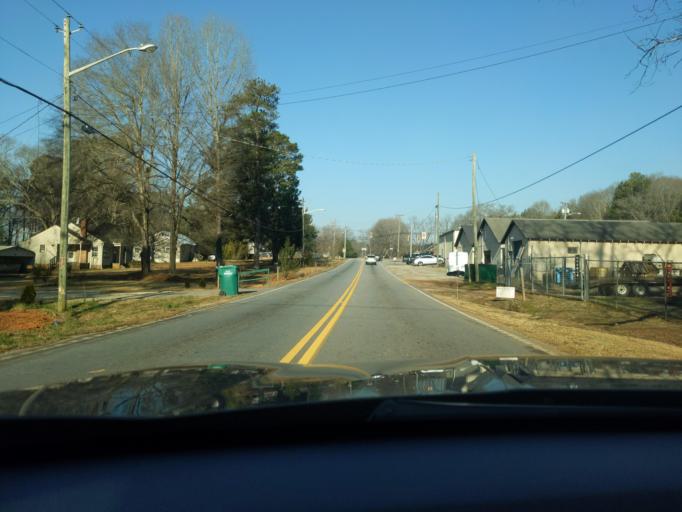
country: US
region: South Carolina
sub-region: Greenwood County
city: Greenwood
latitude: 34.1947
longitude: -82.1293
